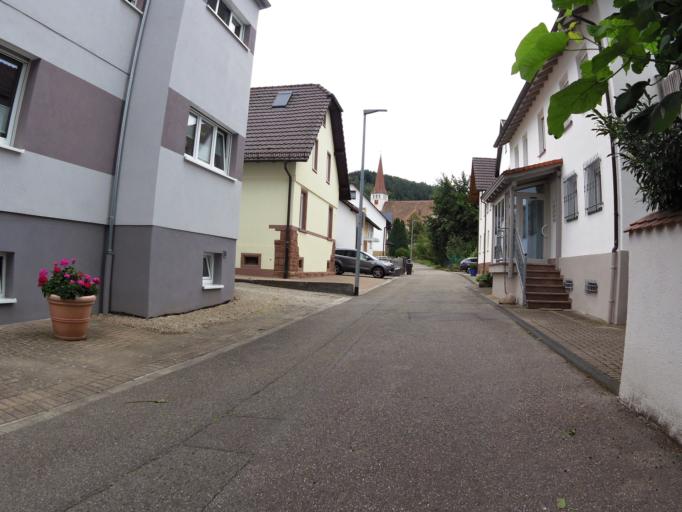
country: DE
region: Baden-Wuerttemberg
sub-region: Freiburg Region
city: Hohberg
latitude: 48.3363
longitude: 7.9110
